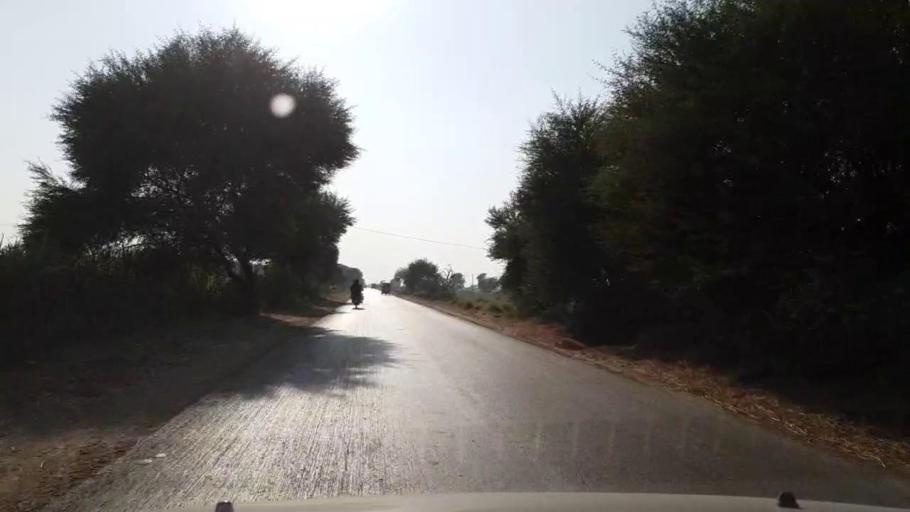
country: PK
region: Sindh
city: Tando Muhammad Khan
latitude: 25.0308
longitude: 68.4255
